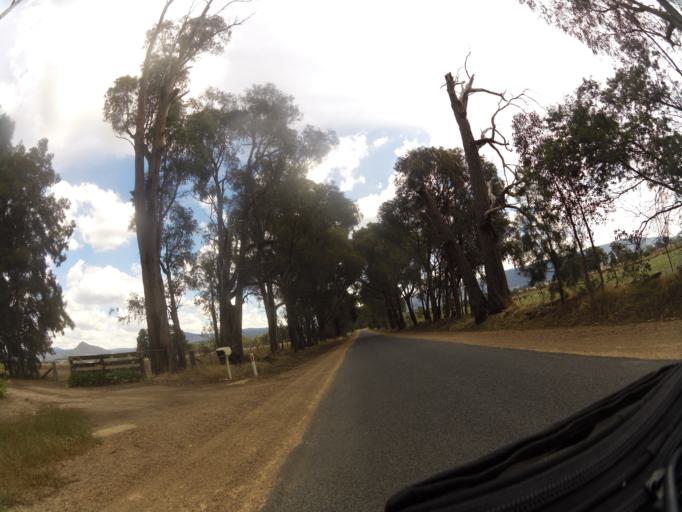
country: AU
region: Victoria
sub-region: Benalla
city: Benalla
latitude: -36.7486
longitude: 145.9899
